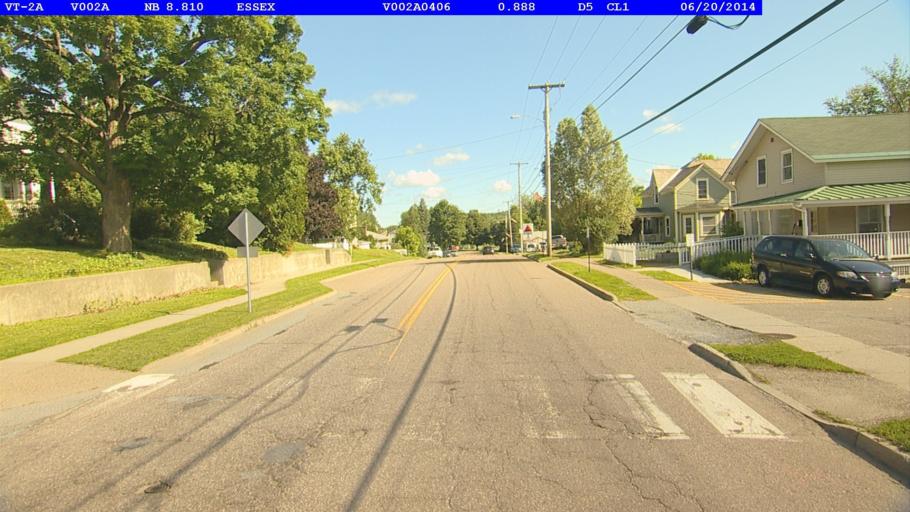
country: US
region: Vermont
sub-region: Chittenden County
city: Essex Junction
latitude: 44.4937
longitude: -73.1114
